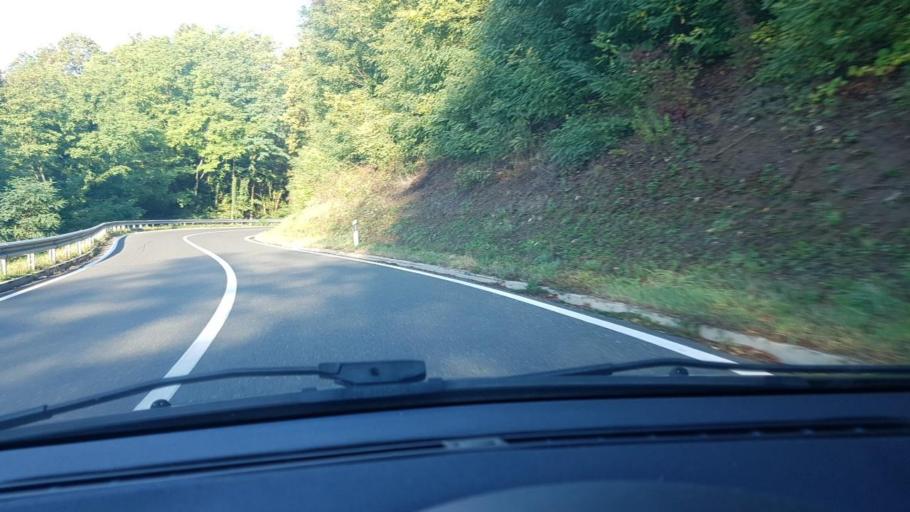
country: HR
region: Krapinsko-Zagorska
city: Marija Bistrica
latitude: 45.9522
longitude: 16.0976
